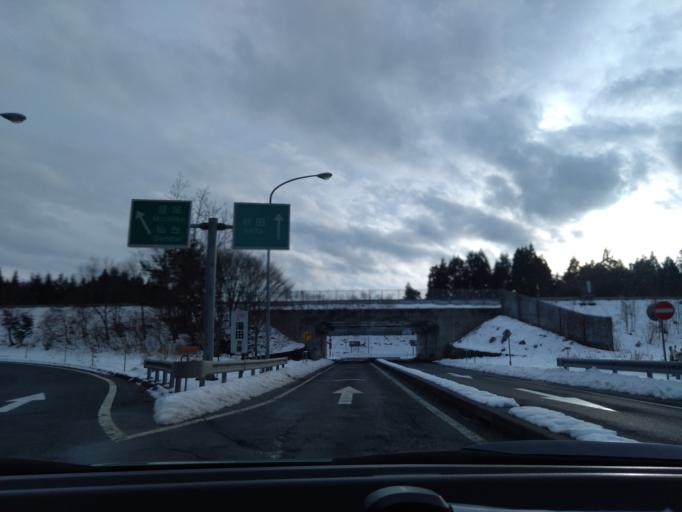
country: JP
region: Iwate
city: Kitakami
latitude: 39.2924
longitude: 140.9848
